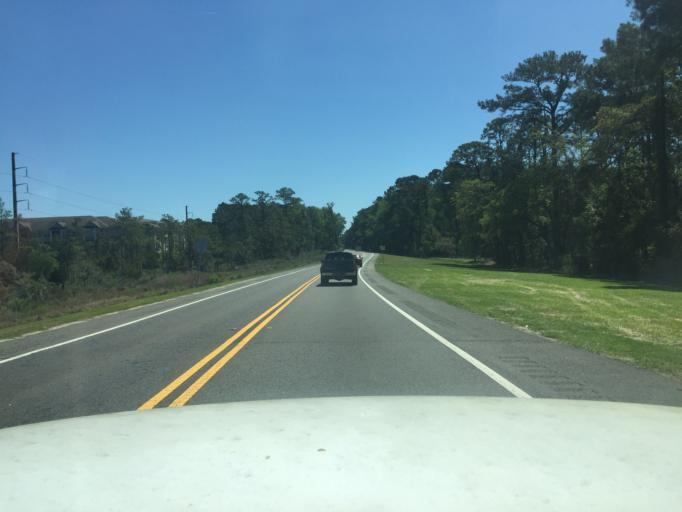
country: US
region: Georgia
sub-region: Chatham County
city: Skidaway Island
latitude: 31.9443
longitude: -81.0617
